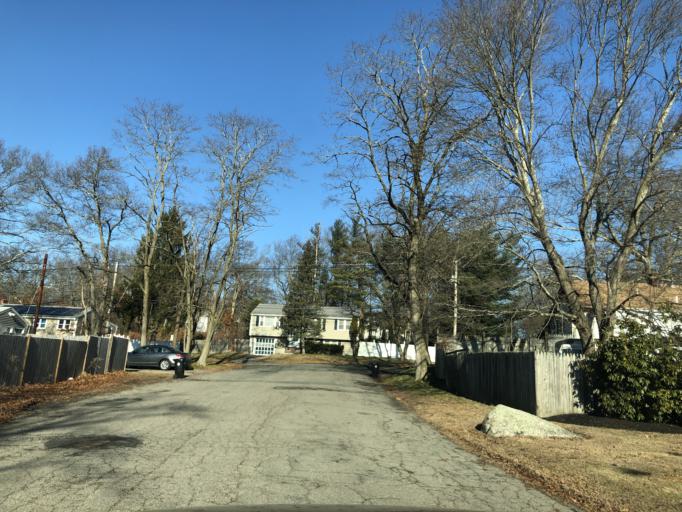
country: US
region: Massachusetts
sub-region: Plymouth County
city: Brockton
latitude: 42.0971
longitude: -71.0018
